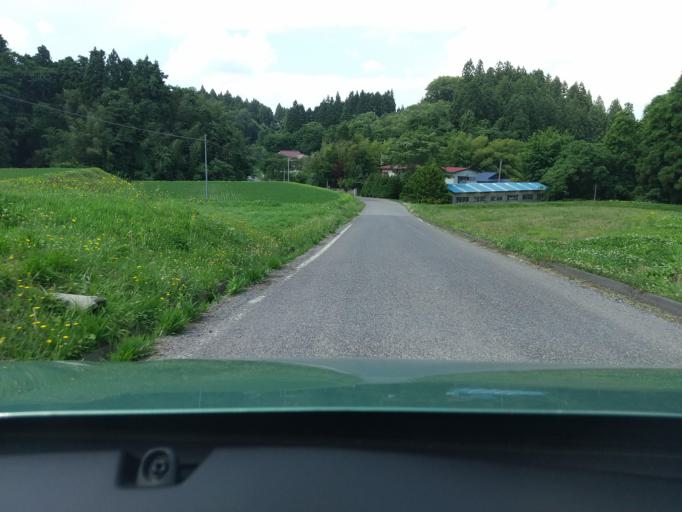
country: JP
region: Iwate
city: Ichinoseki
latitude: 39.0046
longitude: 141.2182
